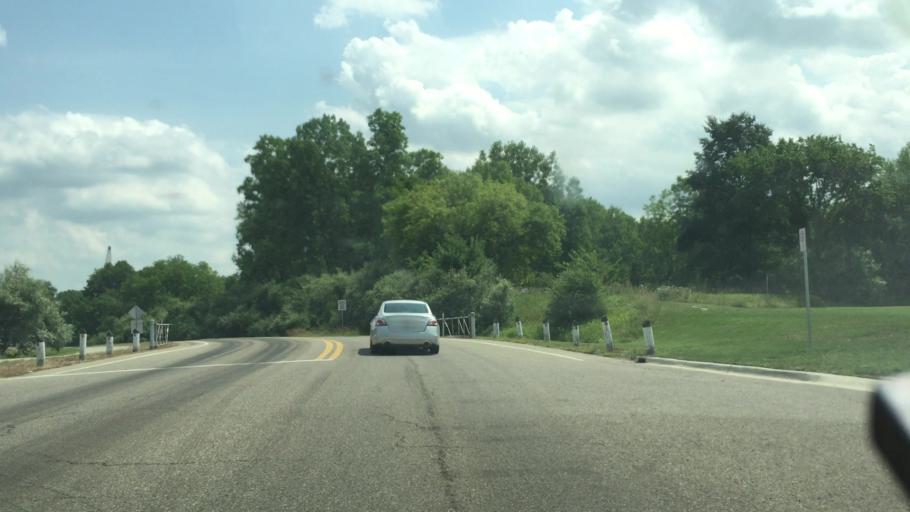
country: US
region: Michigan
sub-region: Oakland County
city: Auburn Hills
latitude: 42.6791
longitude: -83.2075
